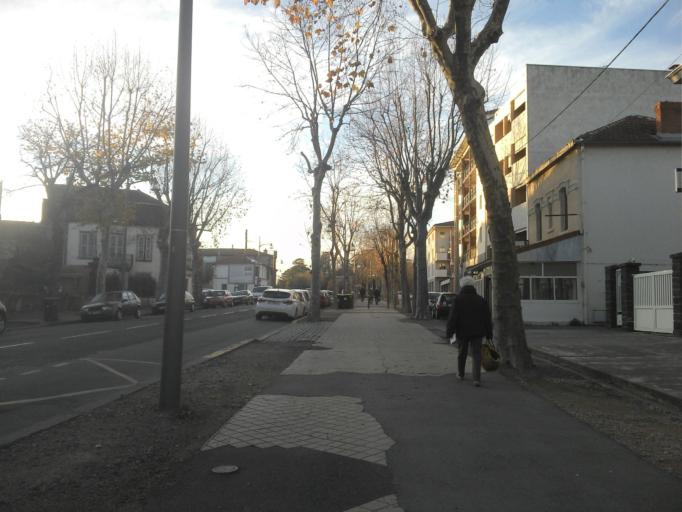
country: FR
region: Auvergne
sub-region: Departement du Puy-de-Dome
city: Riom
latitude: 45.8902
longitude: 3.1194
